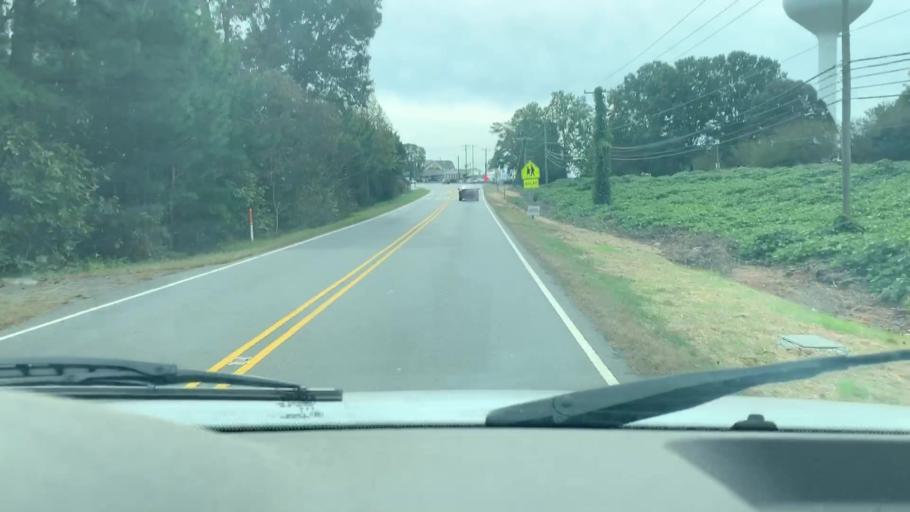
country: US
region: North Carolina
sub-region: Gaston County
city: Davidson
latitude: 35.5500
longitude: -80.8449
